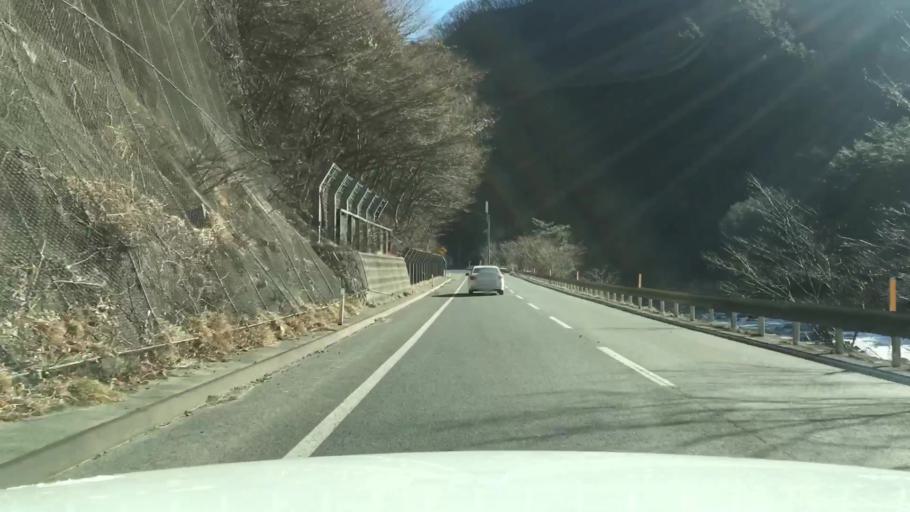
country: JP
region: Iwate
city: Miyako
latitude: 39.5966
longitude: 141.7177
